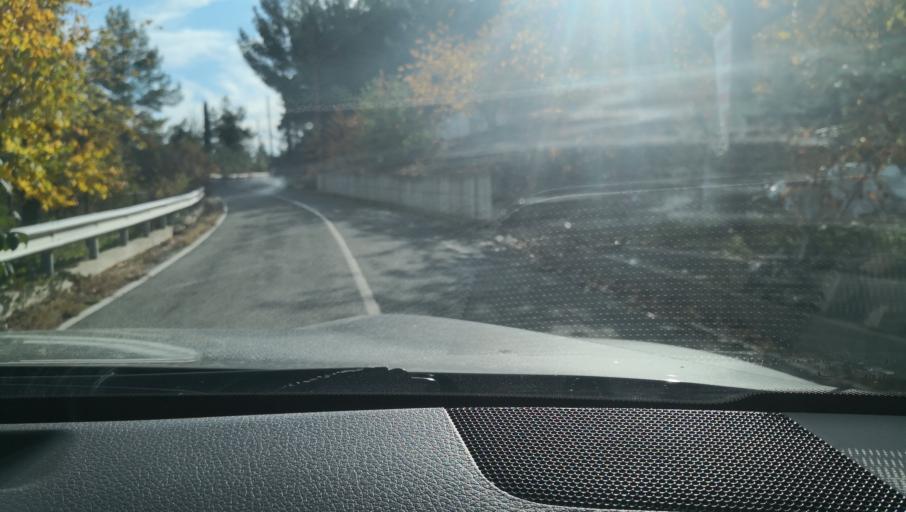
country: CY
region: Lefkosia
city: Lefka
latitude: 35.0159
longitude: 32.7290
